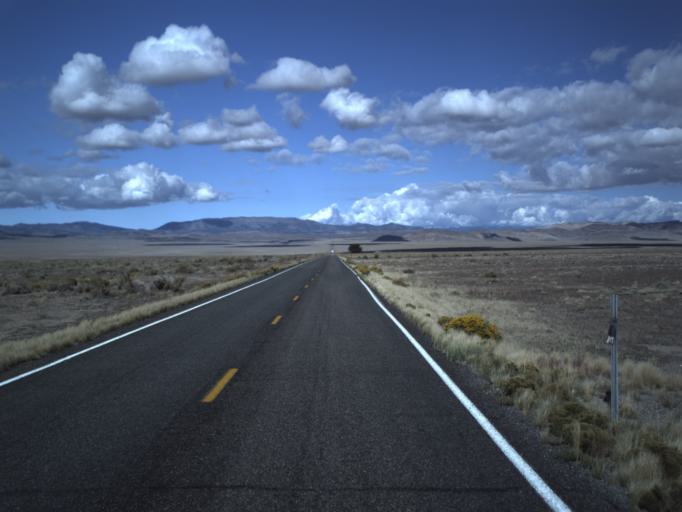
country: US
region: Utah
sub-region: Beaver County
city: Milford
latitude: 38.5308
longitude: -113.6778
